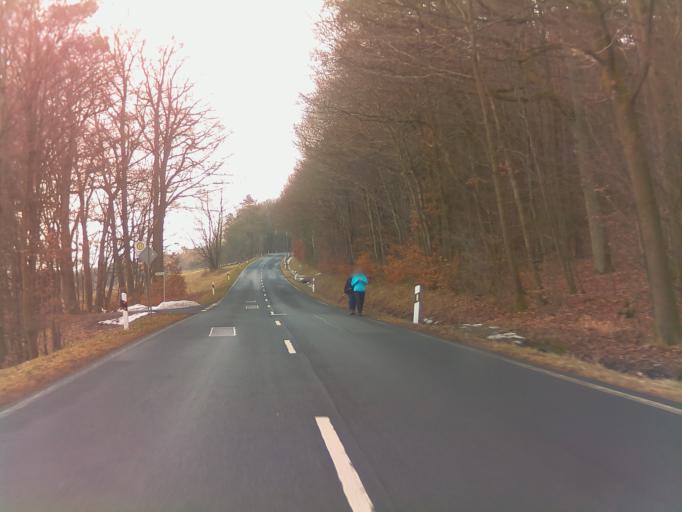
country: DE
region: Bavaria
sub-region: Regierungsbezirk Unterfranken
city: Sandberg
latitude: 50.3334
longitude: 9.9939
